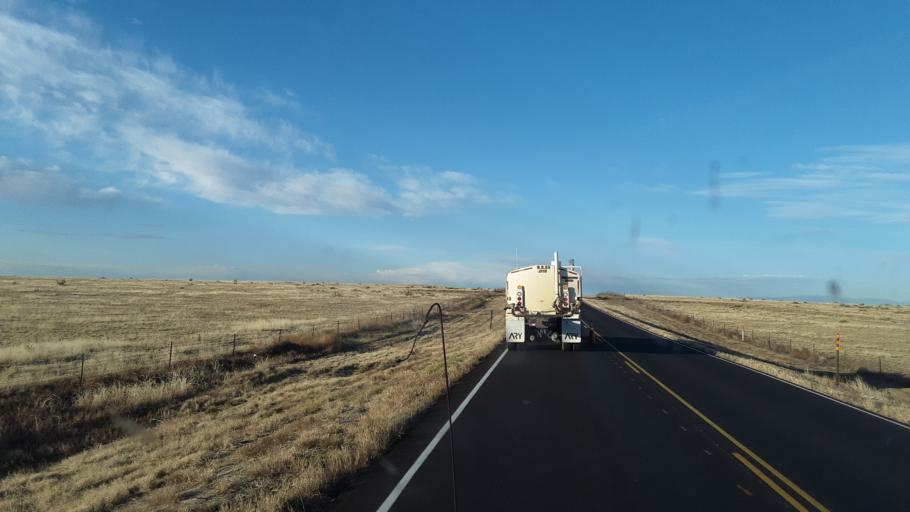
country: US
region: Colorado
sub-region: Otero County
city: Rocky Ford
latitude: 37.9619
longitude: -103.8452
